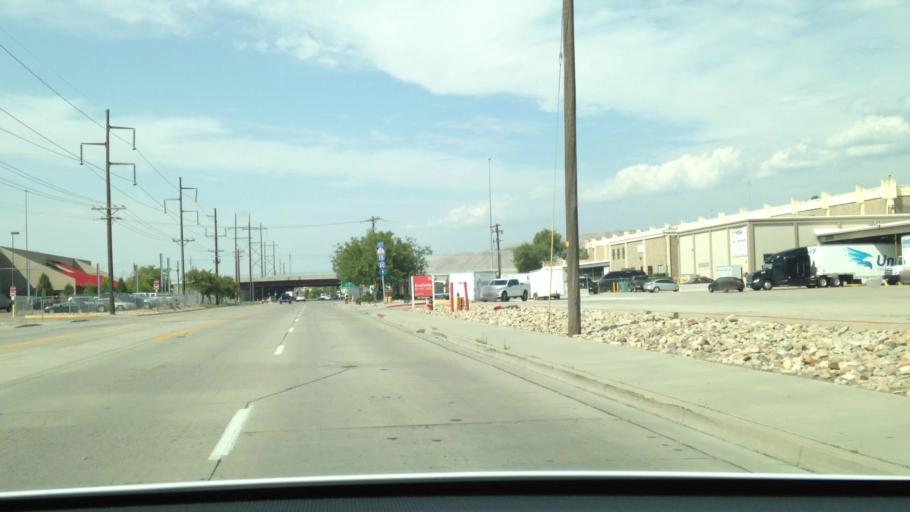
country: US
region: Utah
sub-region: Salt Lake County
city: South Salt Lake
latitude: 40.7207
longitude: -111.9174
